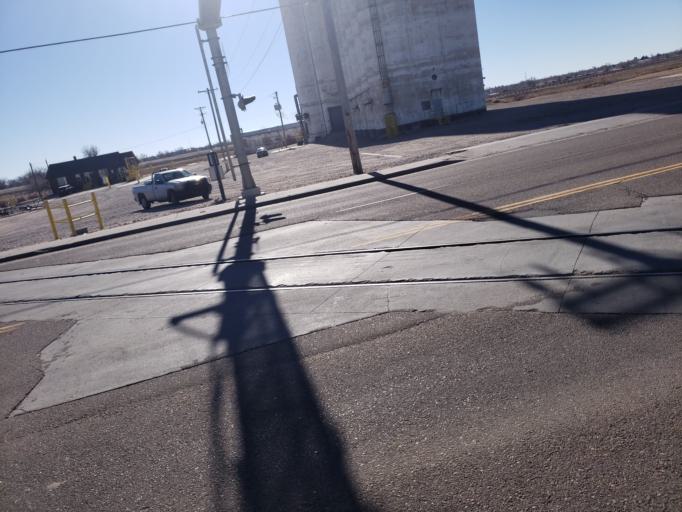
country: US
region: Kansas
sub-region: Ford County
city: Dodge City
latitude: 37.7505
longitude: -100.0097
